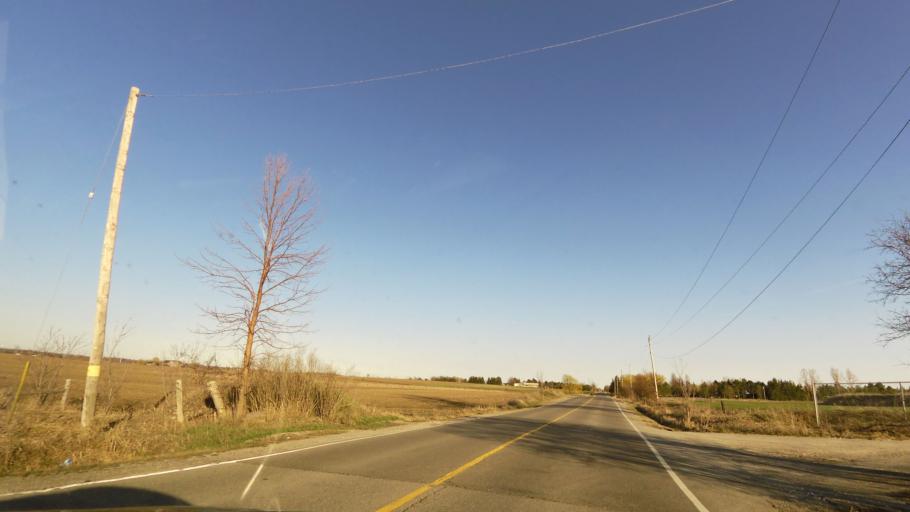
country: CA
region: Ontario
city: Brampton
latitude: 43.8371
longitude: -79.7032
